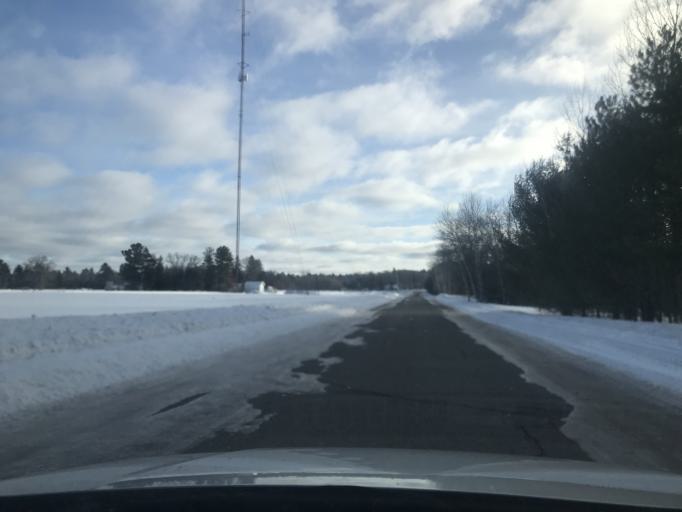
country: US
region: Wisconsin
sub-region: Marinette County
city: Niagara
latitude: 45.6262
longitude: -87.9748
